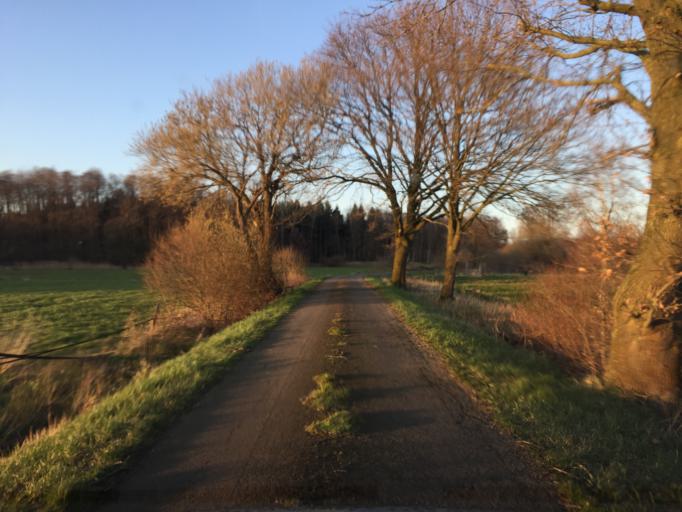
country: DE
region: Lower Saxony
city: Varrel
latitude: 52.6657
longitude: 8.7494
